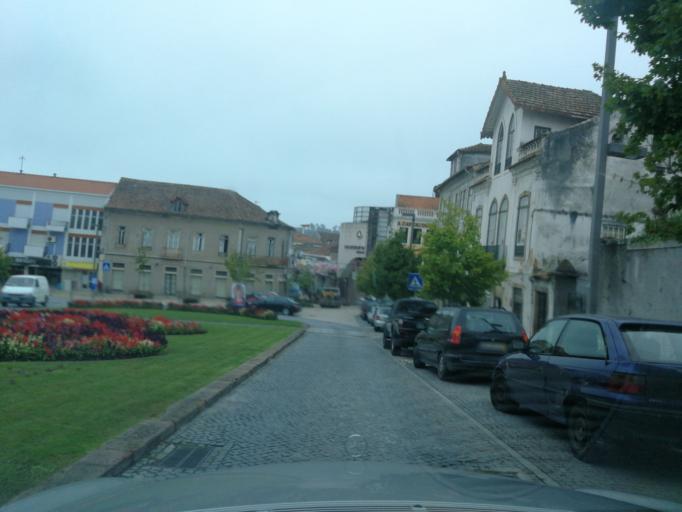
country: PT
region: Aveiro
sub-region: Agueda
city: Agueda
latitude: 40.5731
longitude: -8.4458
